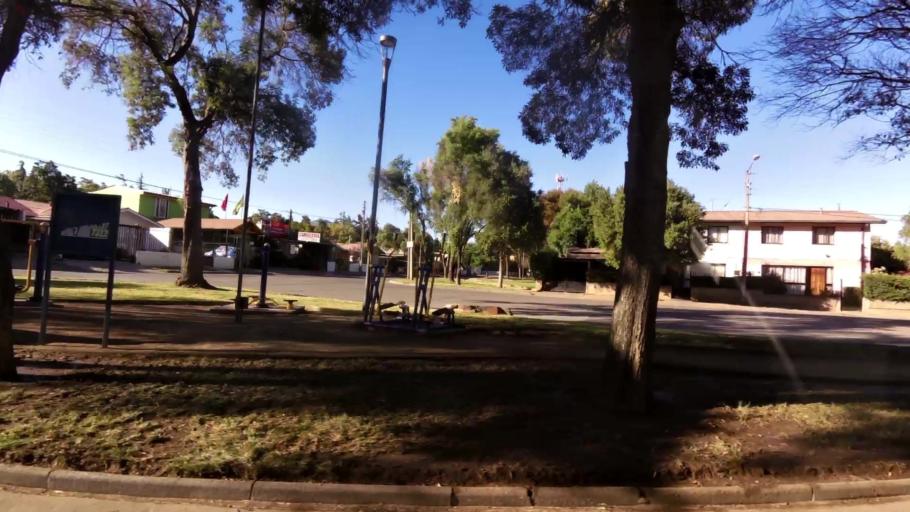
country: CL
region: O'Higgins
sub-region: Provincia de Cachapoal
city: Rancagua
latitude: -34.1777
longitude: -70.7205
